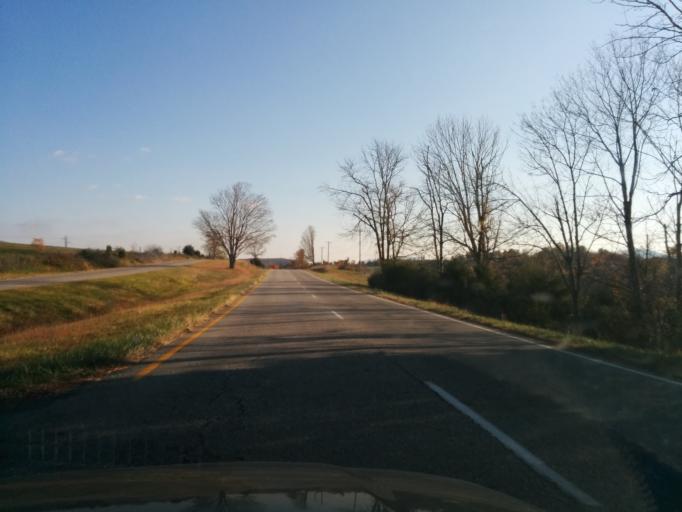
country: US
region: Virginia
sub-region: Rockbridge County
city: East Lexington
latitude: 37.8676
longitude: -79.3101
